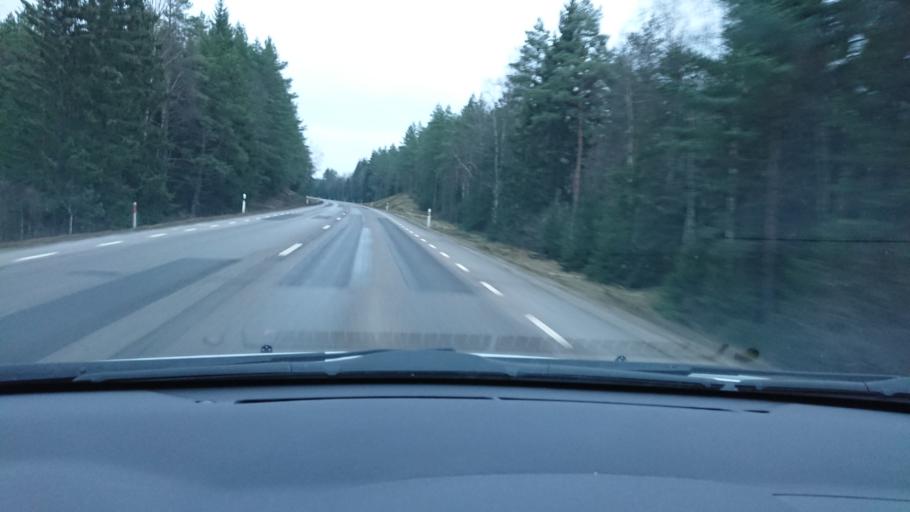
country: SE
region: Kronoberg
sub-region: Vaxjo Kommun
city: Braas
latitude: 57.0689
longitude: 15.1548
